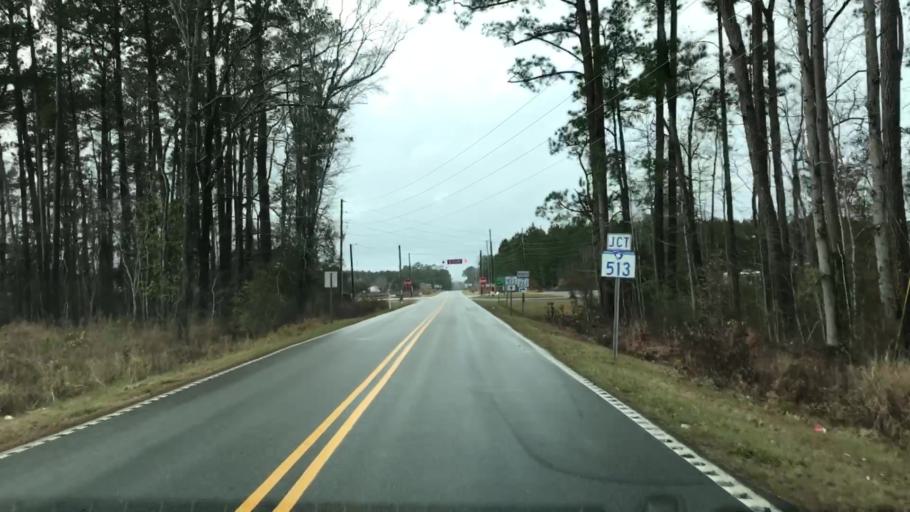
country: US
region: South Carolina
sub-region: Florence County
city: Johnsonville
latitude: 33.6700
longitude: -79.3161
